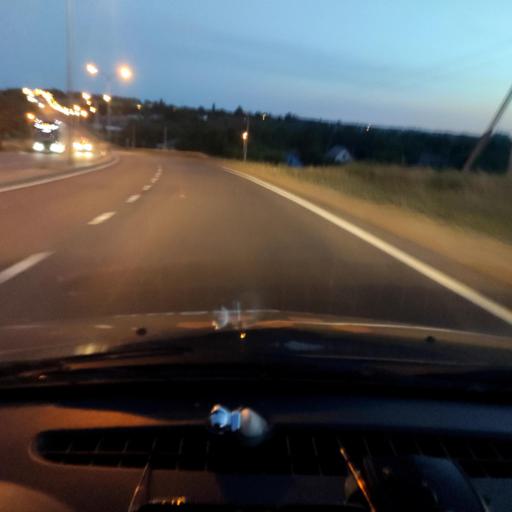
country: RU
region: Belgorod
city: Gubkin
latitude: 51.2601
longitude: 37.5313
